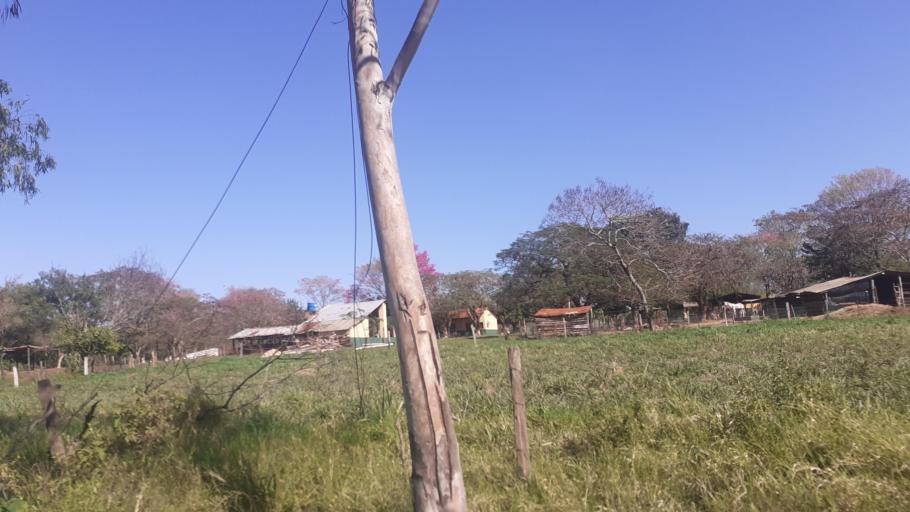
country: PY
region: Misiones
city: San Juan Bautista
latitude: -26.6710
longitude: -57.1249
